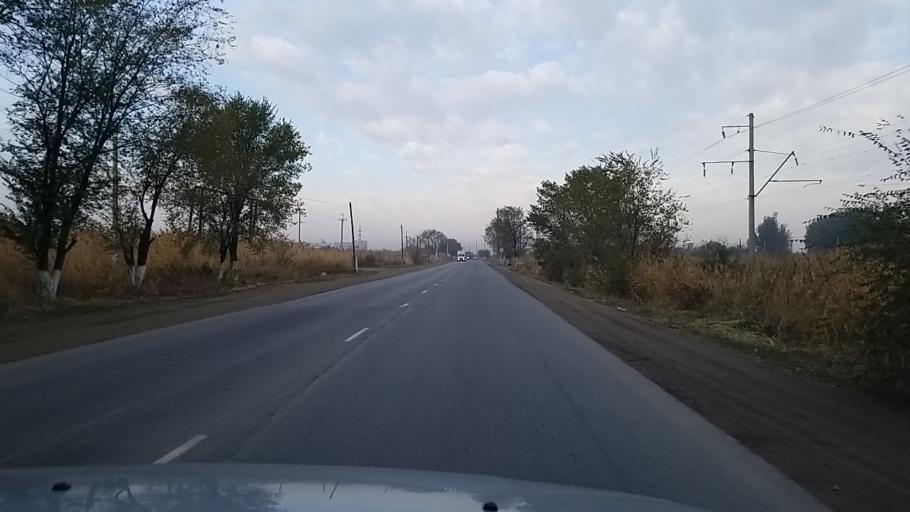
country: KZ
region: Almaty Oblysy
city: Burunday
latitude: 43.3567
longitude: 76.7912
